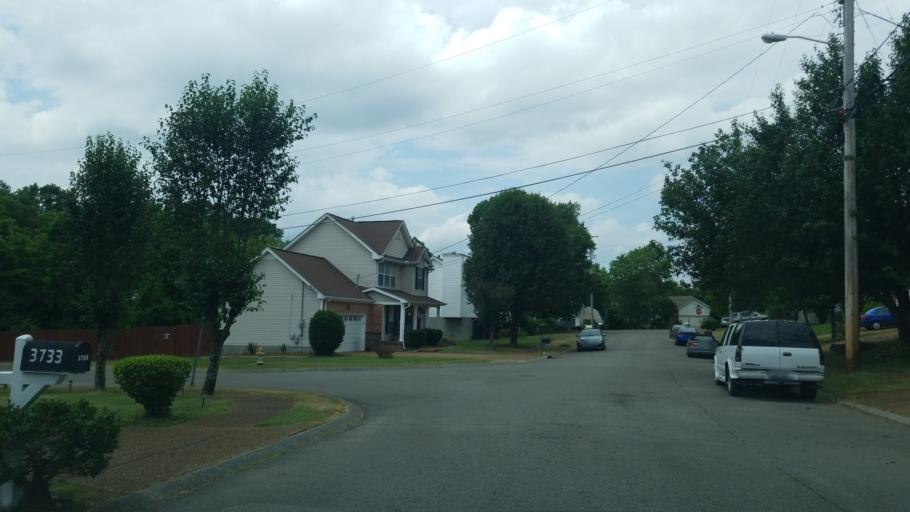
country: US
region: Tennessee
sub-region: Rutherford County
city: La Vergne
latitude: 36.0683
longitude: -86.6010
